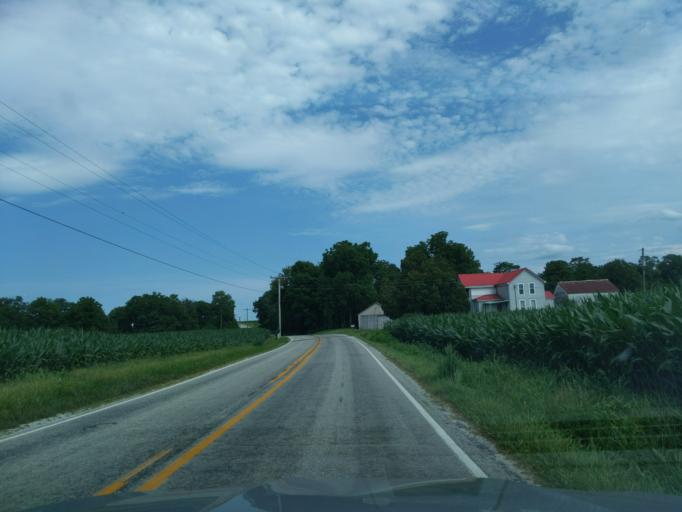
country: US
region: Indiana
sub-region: Ripley County
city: Osgood
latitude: 39.1990
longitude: -85.3028
